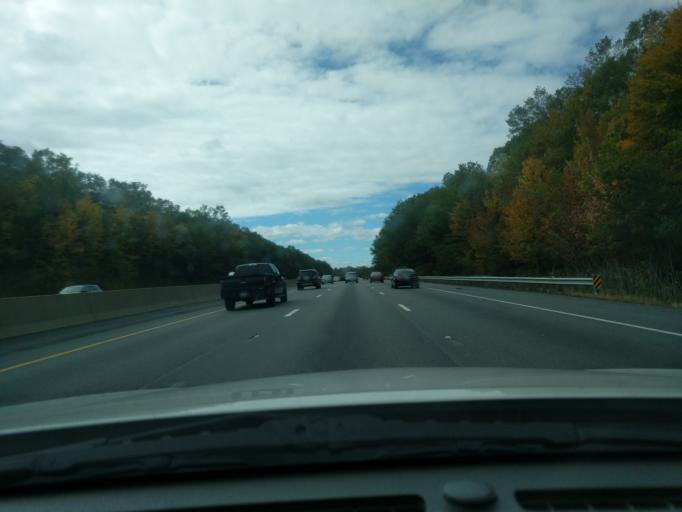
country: US
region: Massachusetts
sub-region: Worcester County
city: Grafton
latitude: 42.2281
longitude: -71.6624
